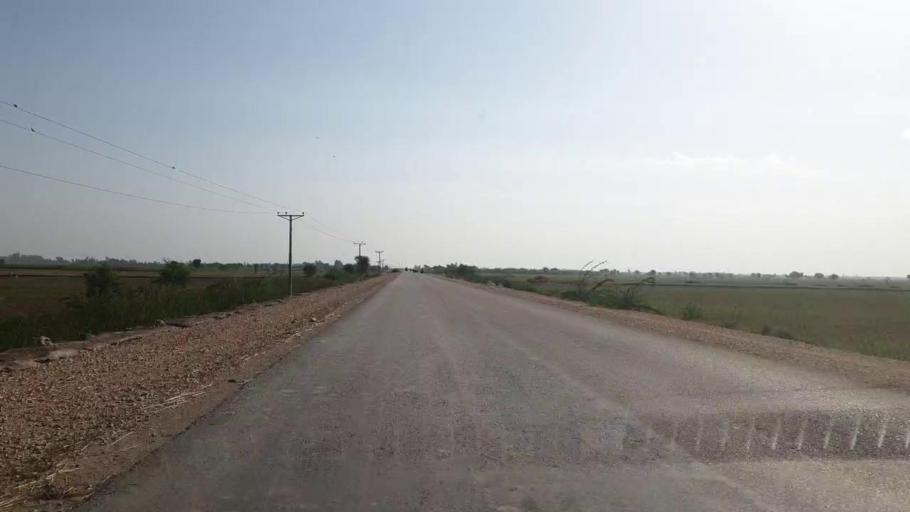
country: PK
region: Sindh
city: Tando Bago
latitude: 24.6573
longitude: 68.9988
